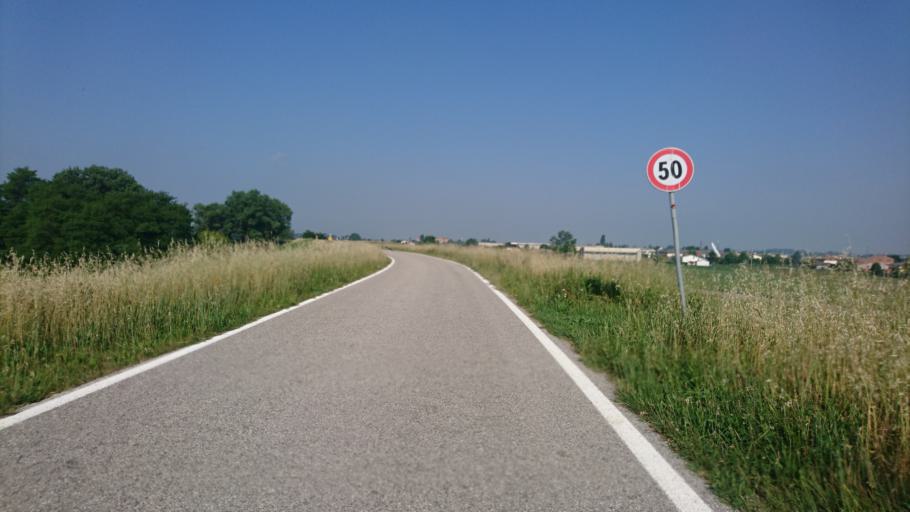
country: IT
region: Lombardy
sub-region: Provincia di Mantova
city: Borgofranco sul Po
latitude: 45.0595
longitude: 11.2163
